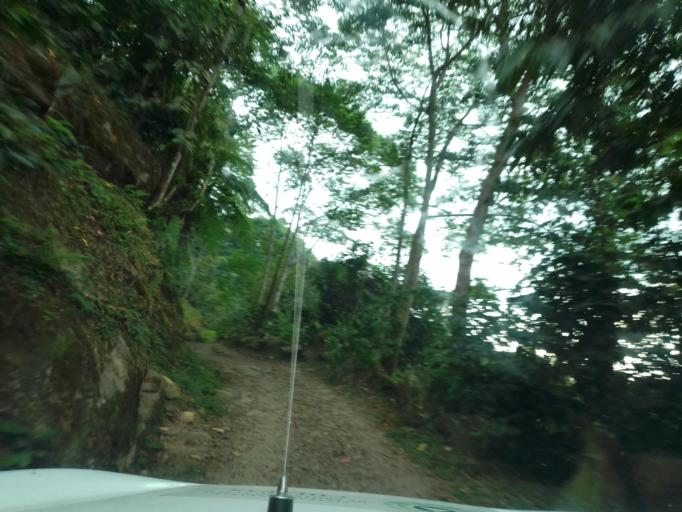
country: MX
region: Chiapas
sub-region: Union Juarez
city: Santo Domingo
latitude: 15.0651
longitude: -92.1244
